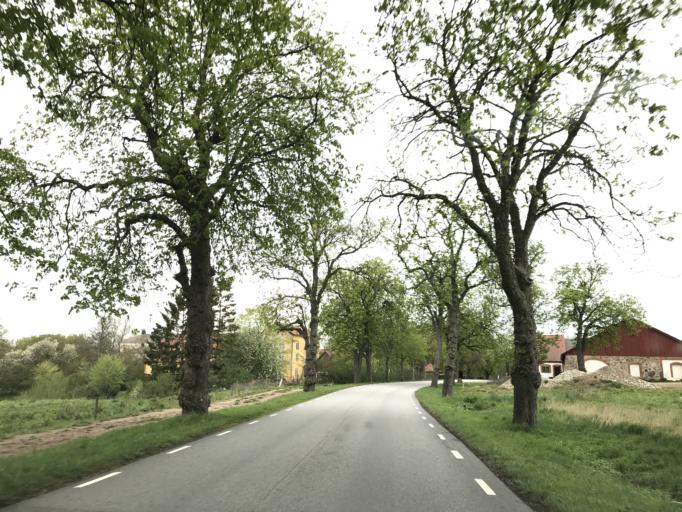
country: SE
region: Skane
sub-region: Trelleborgs Kommun
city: Anderslov
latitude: 55.5051
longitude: 13.3285
